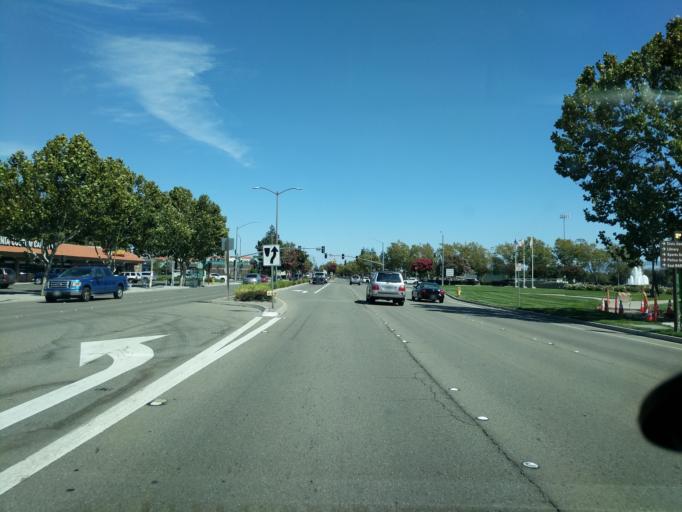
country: US
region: California
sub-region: Alameda County
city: Dublin
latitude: 37.7047
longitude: -121.9170
